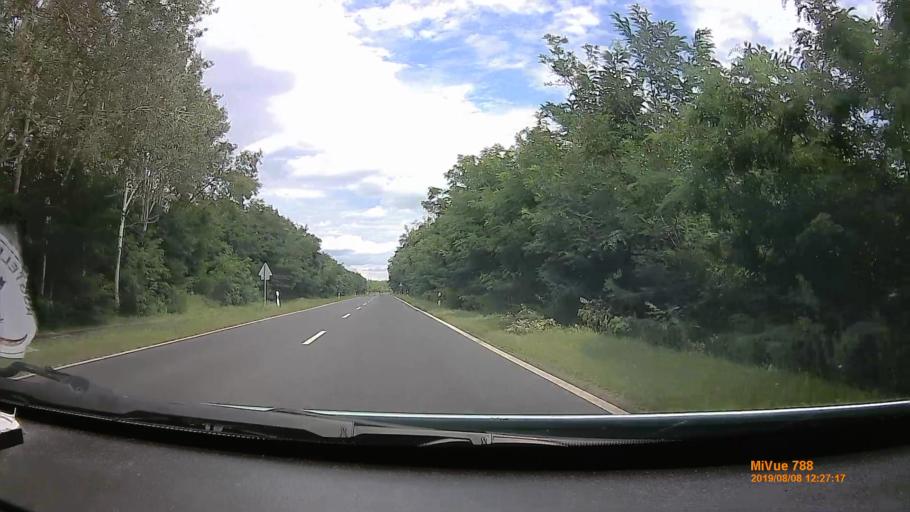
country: HU
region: Szabolcs-Szatmar-Bereg
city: Nyirbogat
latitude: 47.8210
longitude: 22.0967
